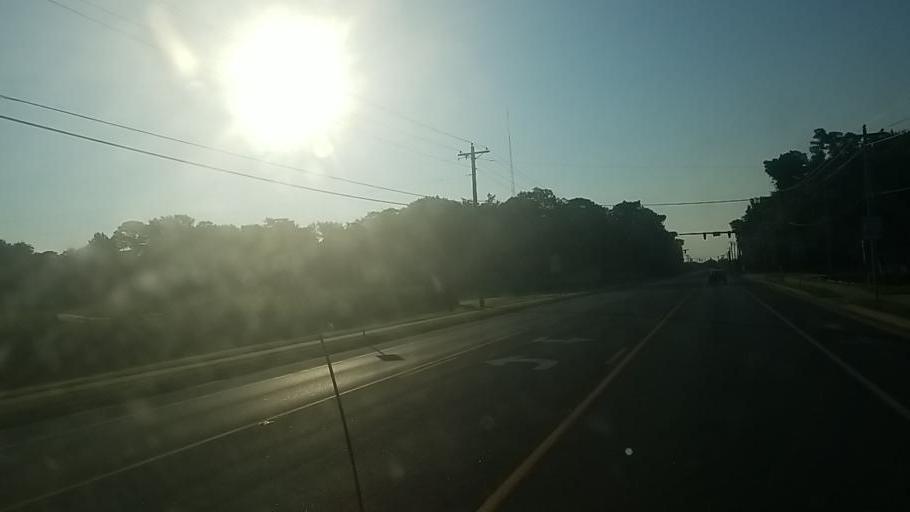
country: US
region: Delaware
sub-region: Sussex County
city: Ocean View
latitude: 38.4727
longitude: -75.0997
